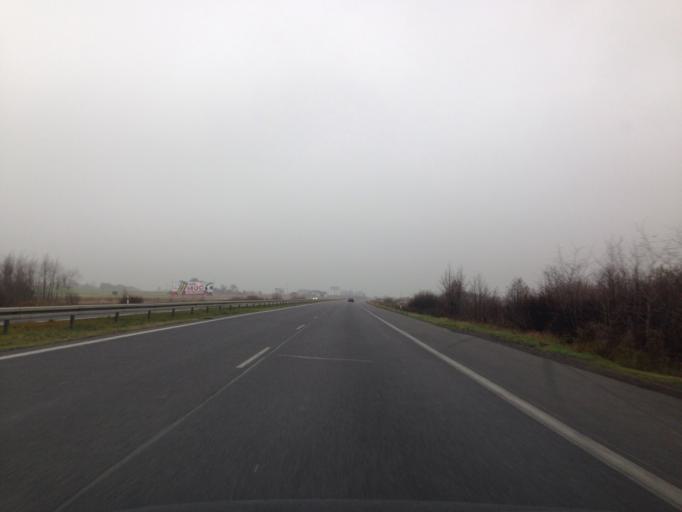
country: PL
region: Lodz Voivodeship
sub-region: Powiat radomszczanski
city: Kamiensk
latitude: 51.2319
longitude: 19.5127
